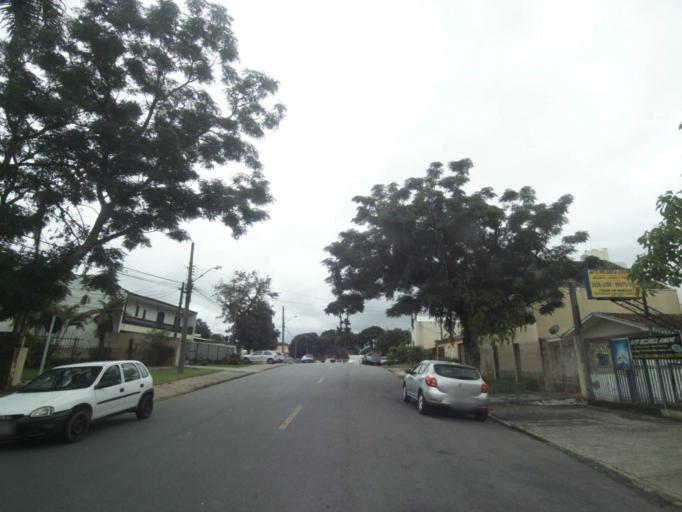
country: BR
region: Parana
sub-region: Curitiba
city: Curitiba
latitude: -25.4888
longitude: -49.2968
